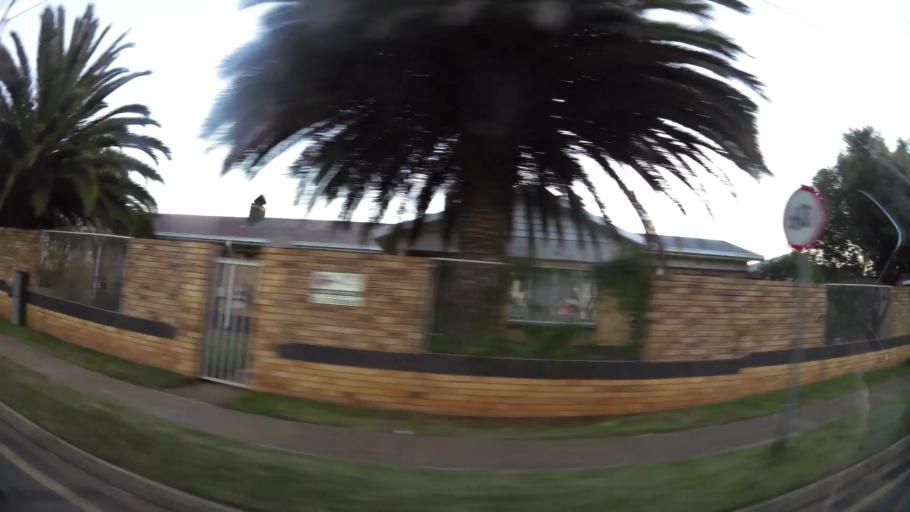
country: ZA
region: Gauteng
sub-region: City of Johannesburg Metropolitan Municipality
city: Roodepoort
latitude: -26.1591
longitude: 27.9001
